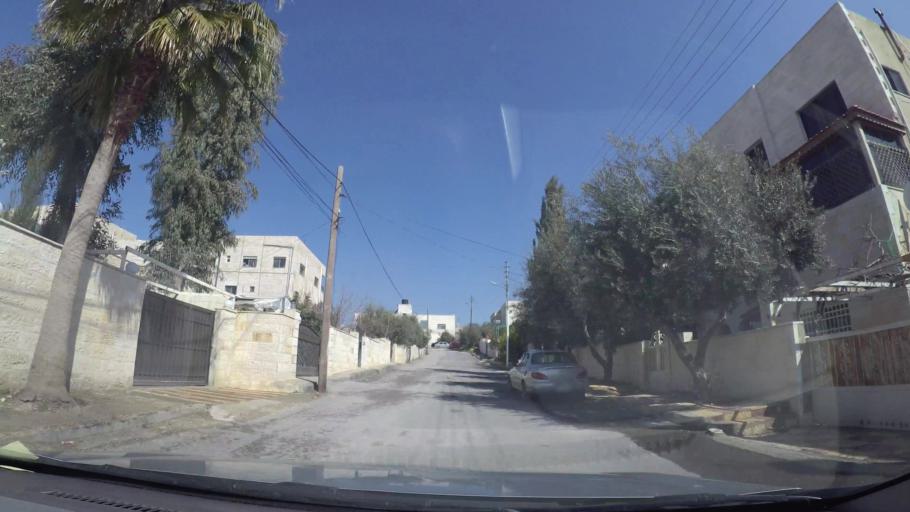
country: JO
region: Amman
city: Al Bunayyat ash Shamaliyah
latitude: 31.8953
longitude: 35.8965
